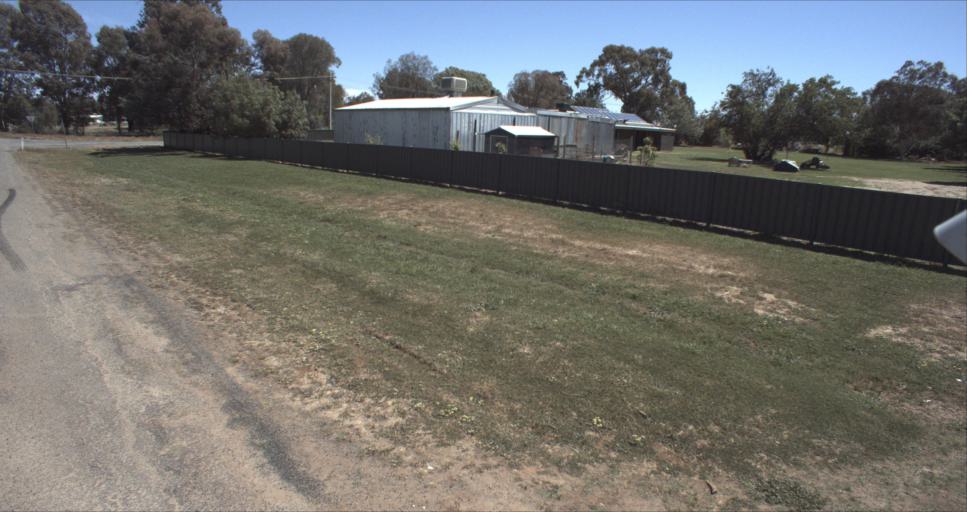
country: AU
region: New South Wales
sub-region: Leeton
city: Leeton
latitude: -34.5253
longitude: 146.3331
